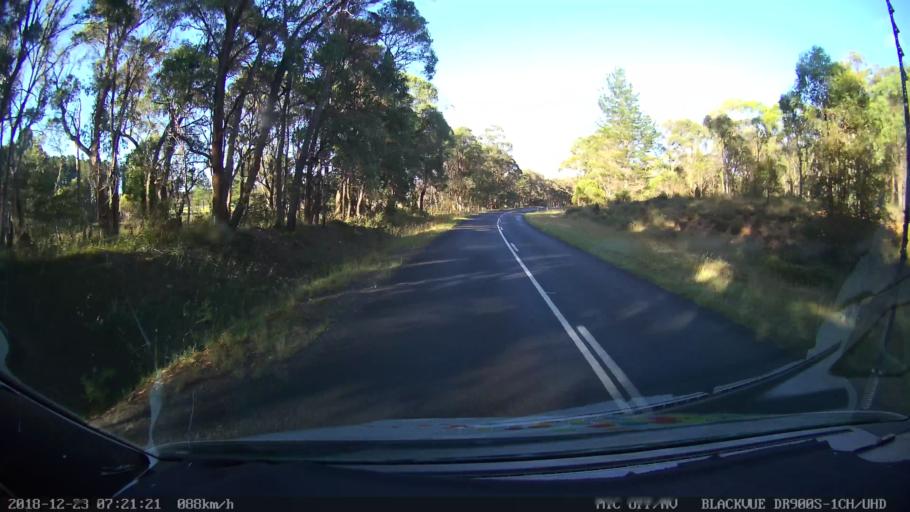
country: AU
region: New South Wales
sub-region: Bellingen
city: Dorrigo
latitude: -30.4970
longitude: 152.2645
